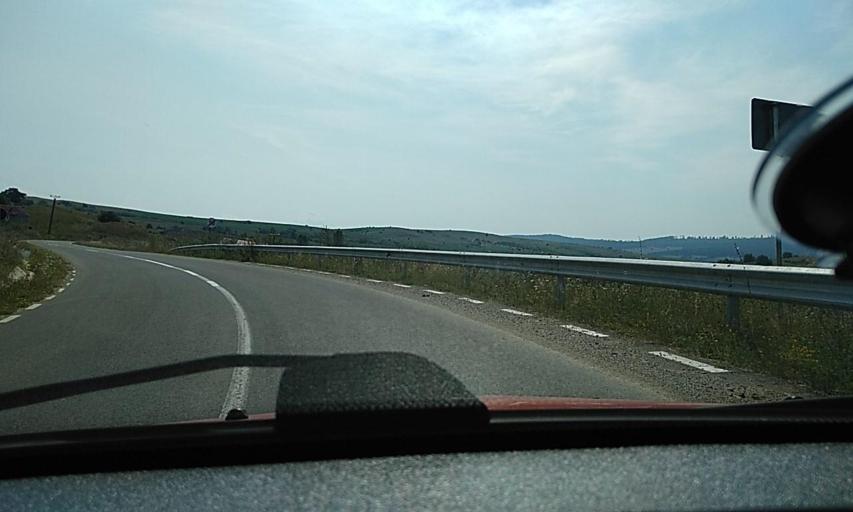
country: RO
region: Brasov
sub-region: Oras Rupea
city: Fiser
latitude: 46.0341
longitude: 25.1372
